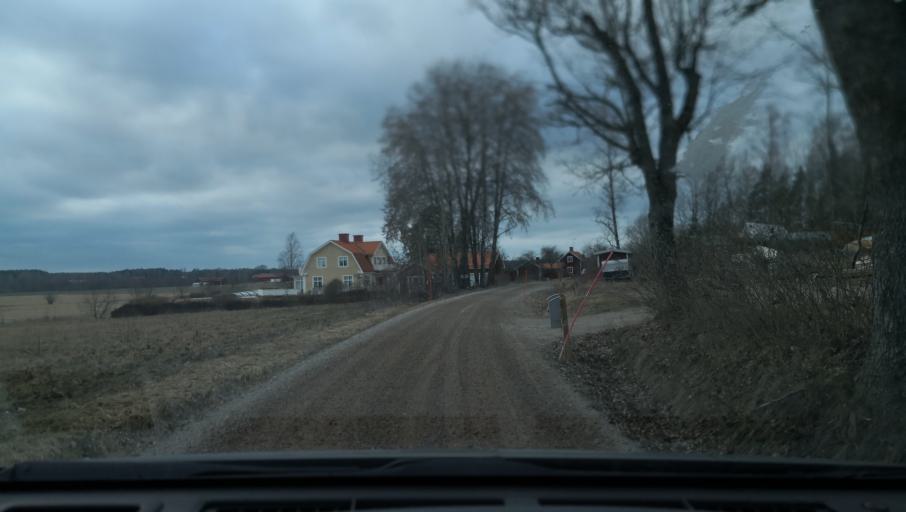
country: SE
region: Vaestmanland
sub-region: Kopings Kommun
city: Koping
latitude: 59.5295
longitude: 15.9063
